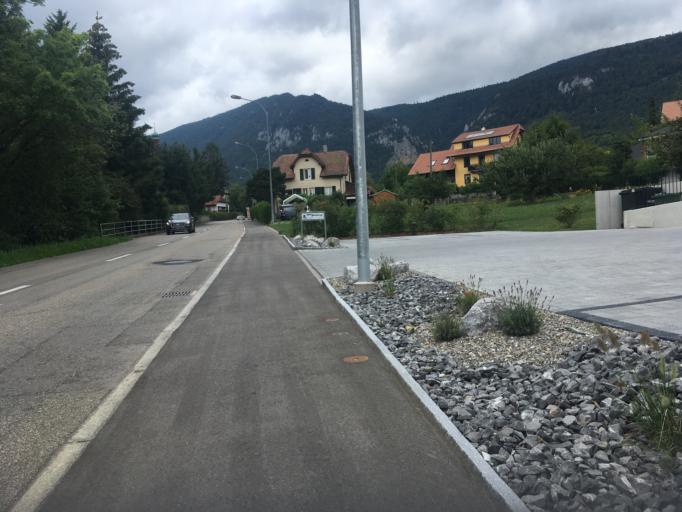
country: CH
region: Solothurn
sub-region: Bezirk Lebern
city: Langendorf
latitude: 47.2283
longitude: 7.5065
